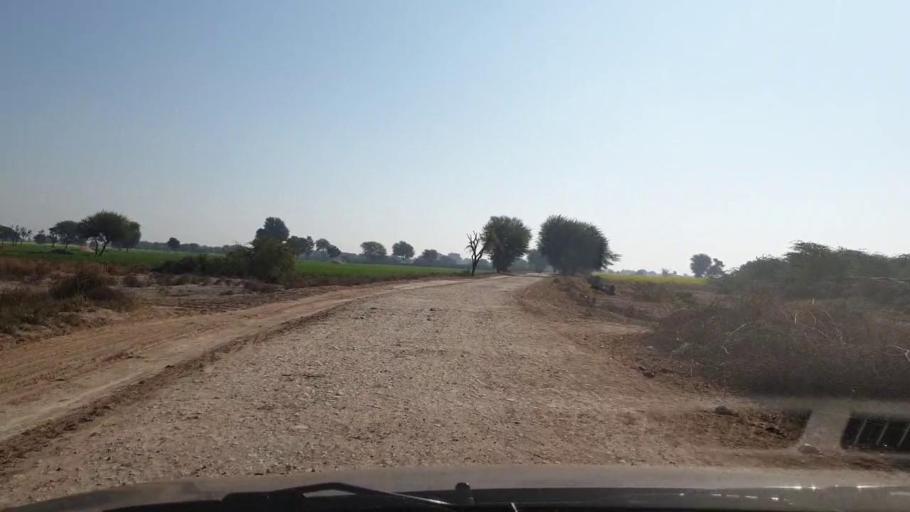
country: PK
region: Sindh
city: Jhol
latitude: 25.9359
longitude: 68.8218
